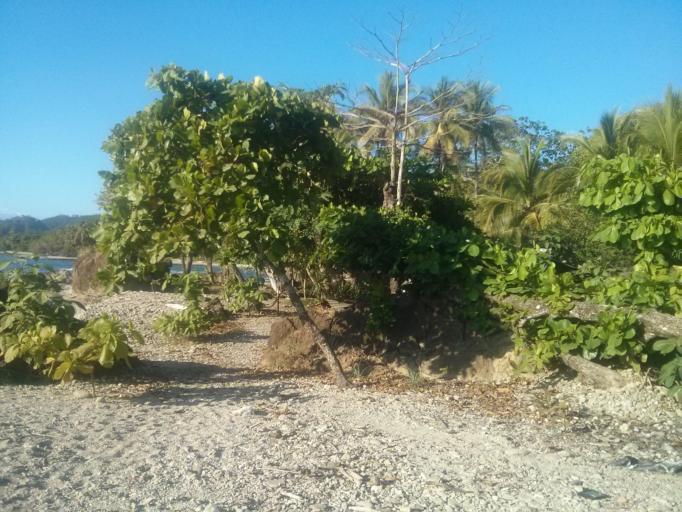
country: CR
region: Puntarenas
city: Paquera
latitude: 9.6139
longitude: -85.1442
